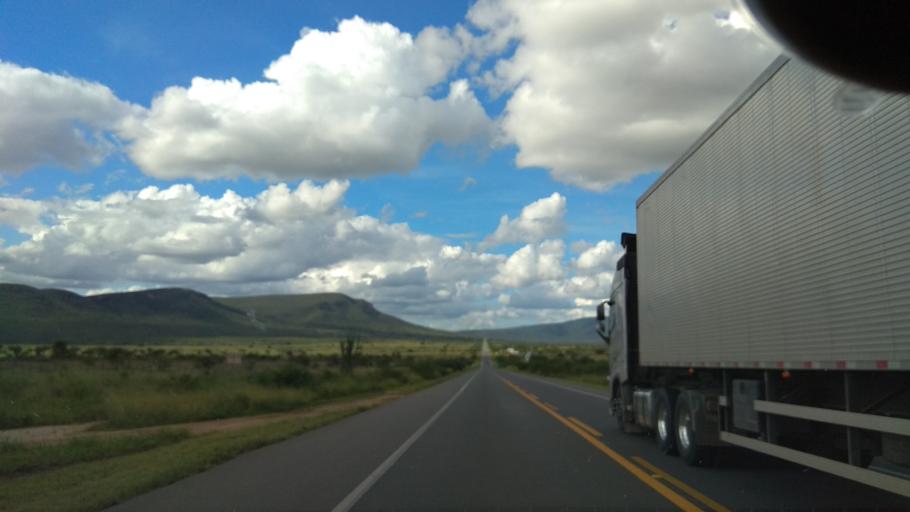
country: BR
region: Bahia
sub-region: Castro Alves
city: Castro Alves
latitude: -12.6737
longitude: -39.6567
